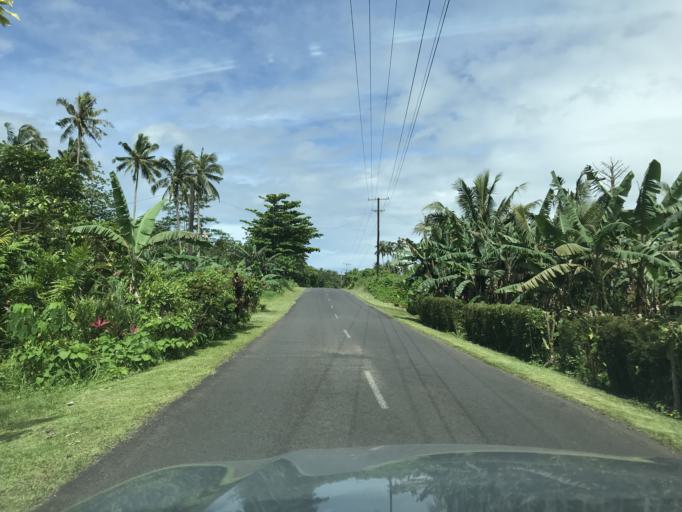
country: WS
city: Fasito`outa
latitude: -13.8578
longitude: -171.8982
